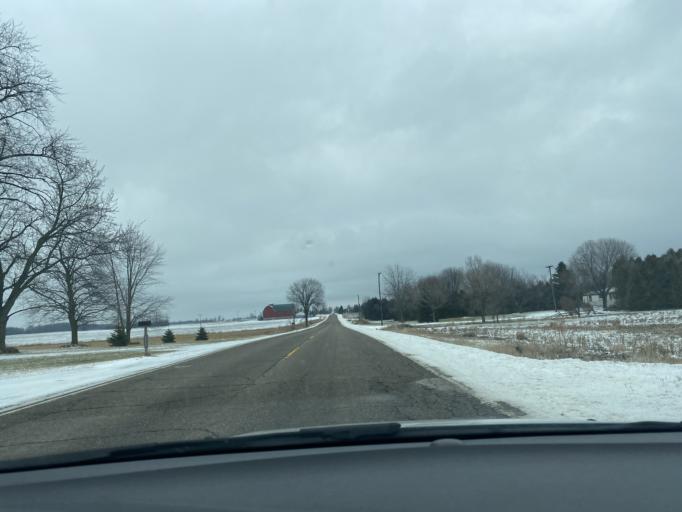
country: US
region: Michigan
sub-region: Lapeer County
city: North Branch
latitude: 43.2101
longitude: -83.1046
